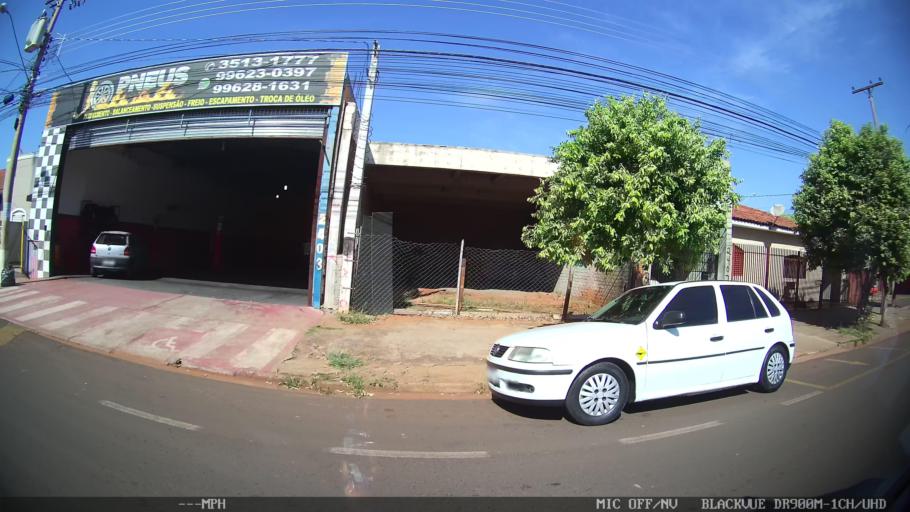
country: BR
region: Sao Paulo
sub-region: Sao Jose Do Rio Preto
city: Sao Jose do Rio Preto
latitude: -20.7841
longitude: -49.3965
